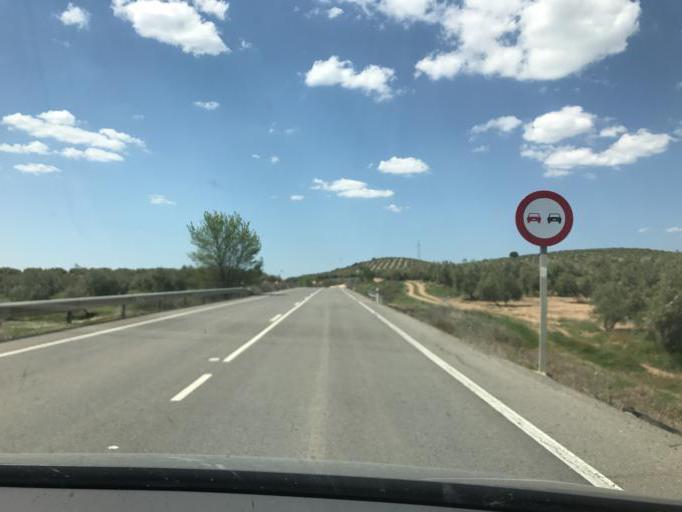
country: ES
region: Andalusia
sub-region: Provincia de Jaen
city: Frailes
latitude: 37.4393
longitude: -3.8192
